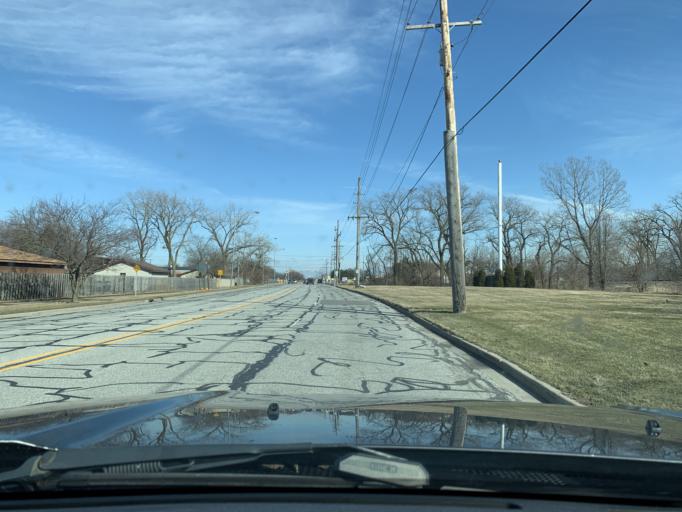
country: US
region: Indiana
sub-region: Lake County
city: Munster
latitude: 41.5377
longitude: -87.4937
